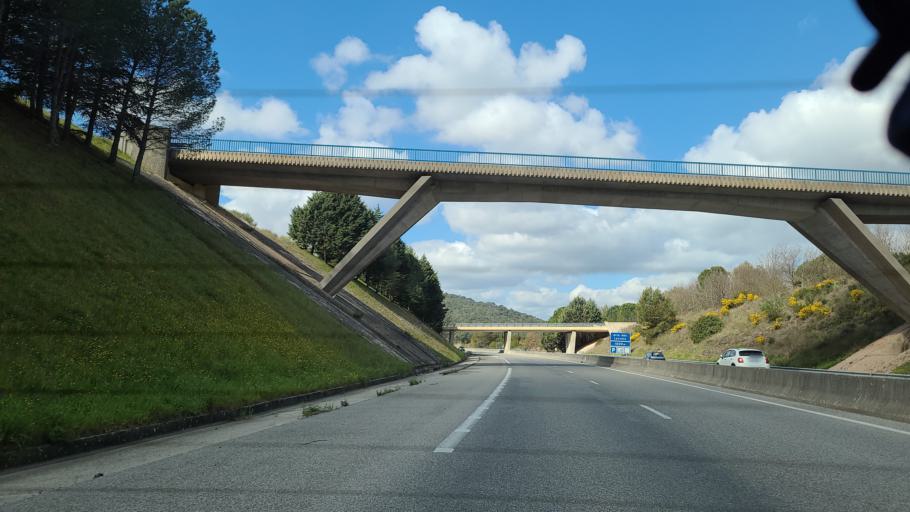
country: FR
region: Provence-Alpes-Cote d'Azur
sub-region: Departement du Var
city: Carnoules
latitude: 43.2911
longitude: 6.2016
